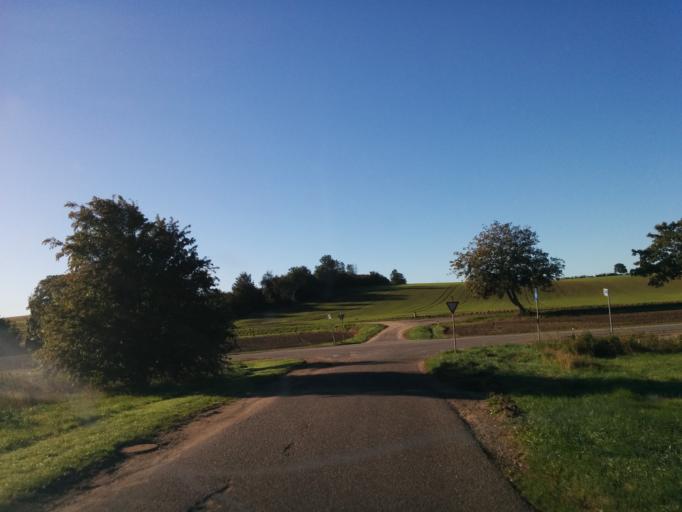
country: DK
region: South Denmark
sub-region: Kolding Kommune
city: Sonder Bjert
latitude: 55.4585
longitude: 9.5475
